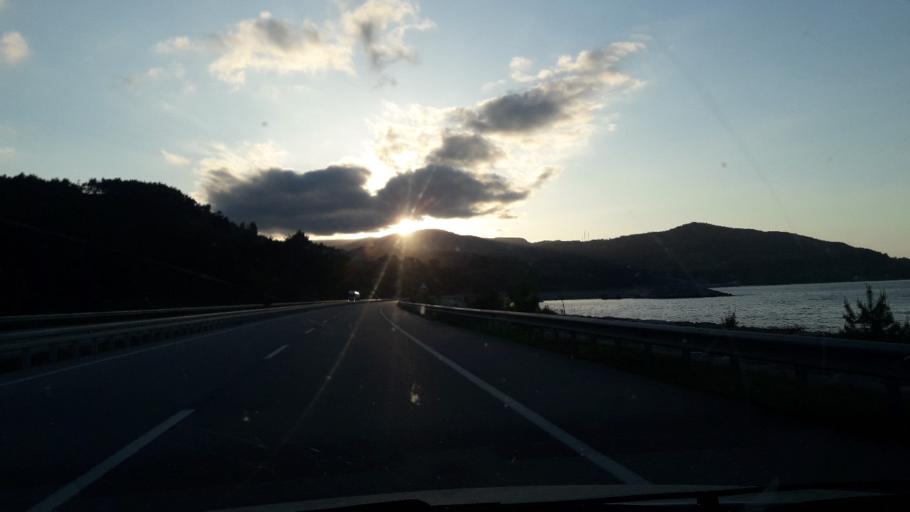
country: TR
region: Sinop
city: Dikmen
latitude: 41.7134
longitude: 35.2831
